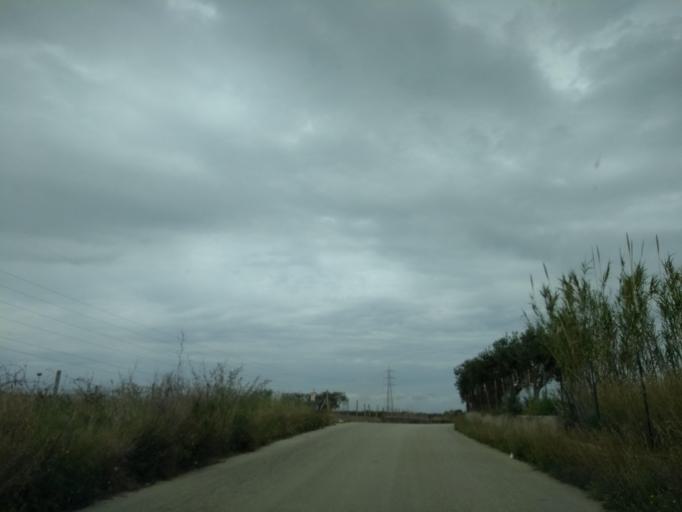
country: IT
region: Sicily
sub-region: Palermo
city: Partinico
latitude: 37.9923
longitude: 13.0669
